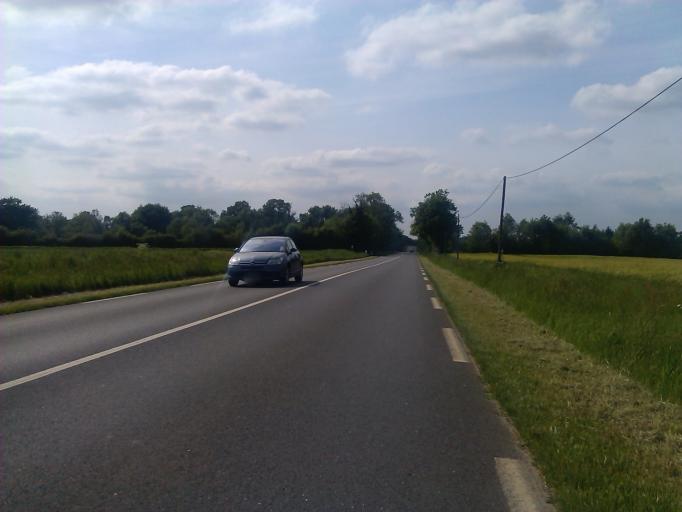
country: FR
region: Centre
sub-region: Departement de l'Indre
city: La Chatre
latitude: 46.5744
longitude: 2.0184
